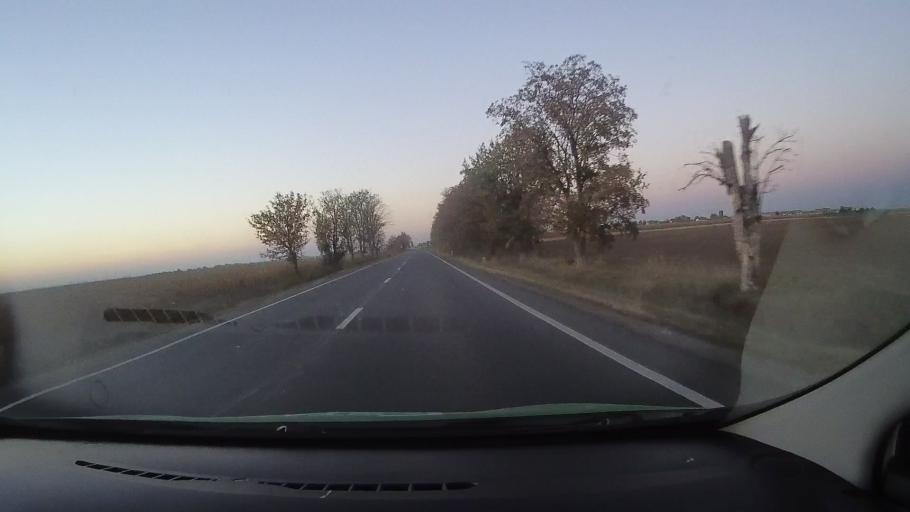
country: RO
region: Bihor
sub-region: Comuna Tarcea
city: Tarcea
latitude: 47.4760
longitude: 22.1639
